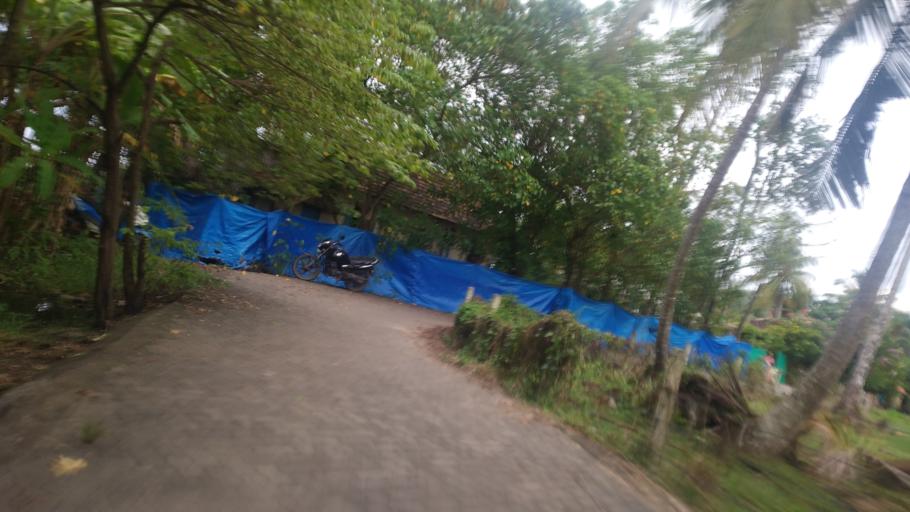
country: IN
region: Kerala
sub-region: Ernakulam
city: Cochin
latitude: 9.8723
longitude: 76.2749
